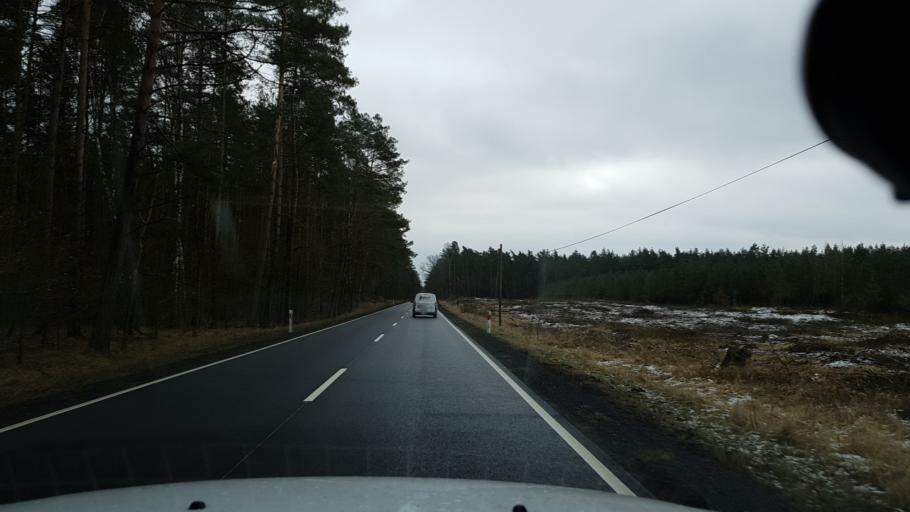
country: PL
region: West Pomeranian Voivodeship
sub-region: Powiat goleniowski
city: Stepnica
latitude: 53.6315
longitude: 14.6697
